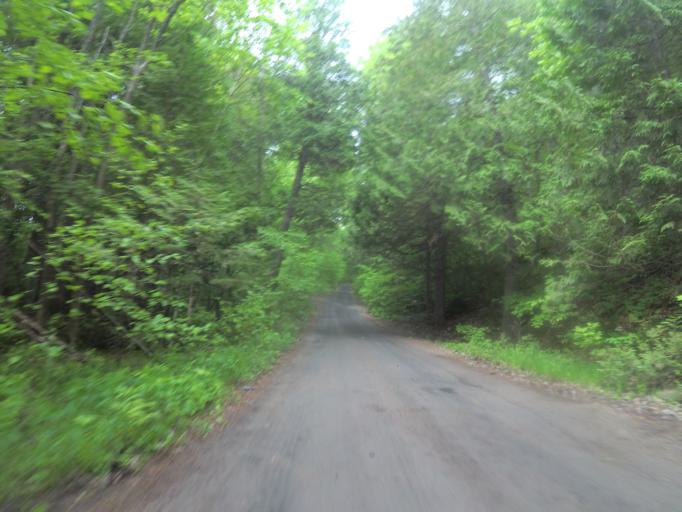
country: CA
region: Ontario
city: Renfrew
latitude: 45.1051
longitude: -76.8258
